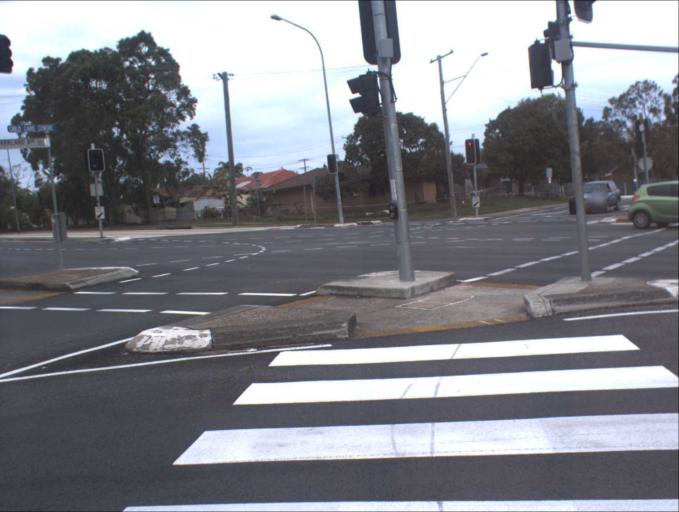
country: AU
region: Queensland
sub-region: Brisbane
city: Sunnybank Hills
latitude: -27.6623
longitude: 153.0526
